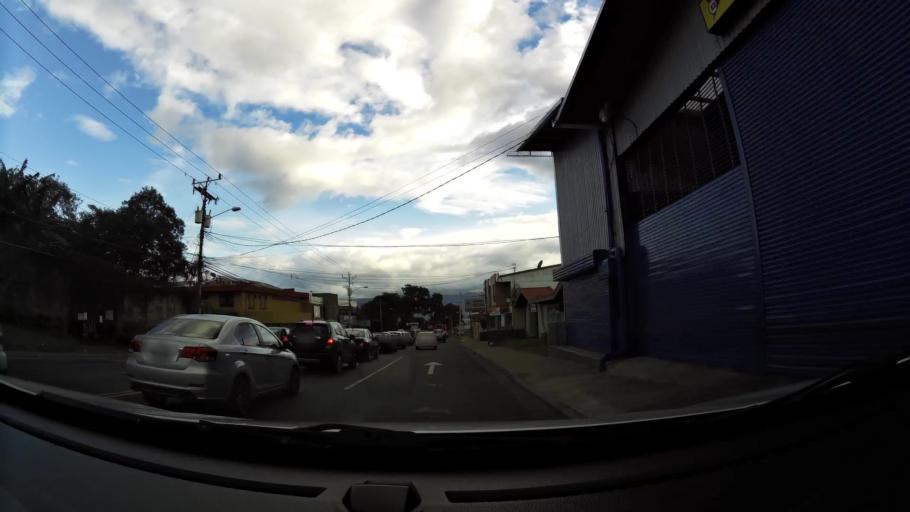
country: CR
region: Alajuela
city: Alajuela
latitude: 10.0115
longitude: -84.2098
